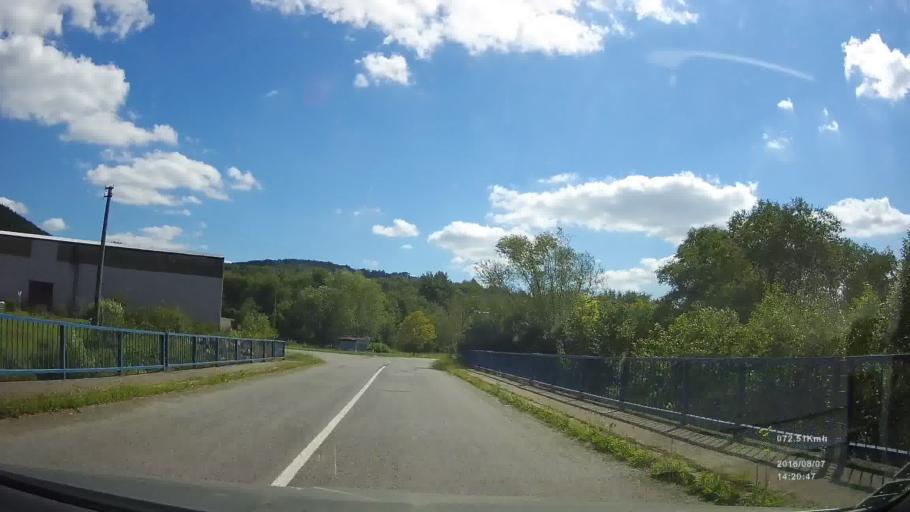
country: SK
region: Presovsky
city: Stropkov
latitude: 49.2860
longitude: 21.7609
